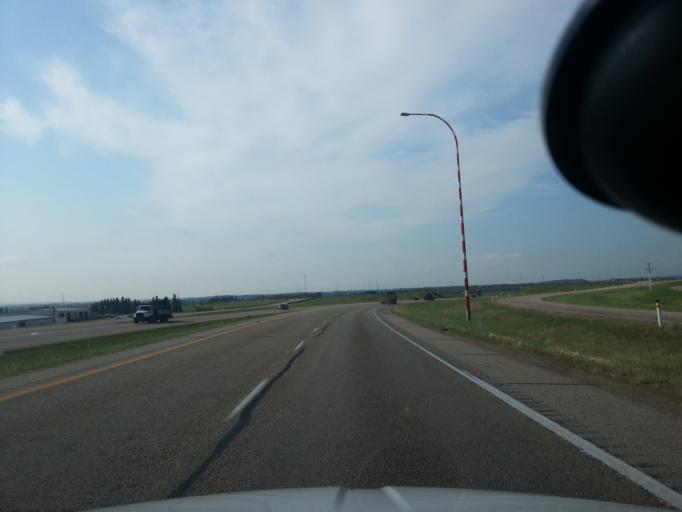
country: CA
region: Alberta
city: Blackfalds
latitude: 52.3794
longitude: -113.8198
